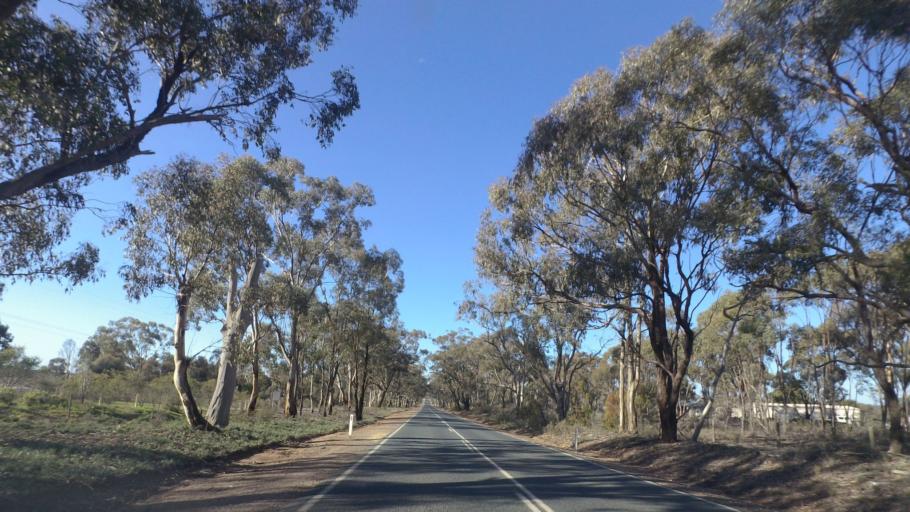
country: AU
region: Victoria
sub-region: Greater Bendigo
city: Epsom
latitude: -36.6766
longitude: 144.3897
